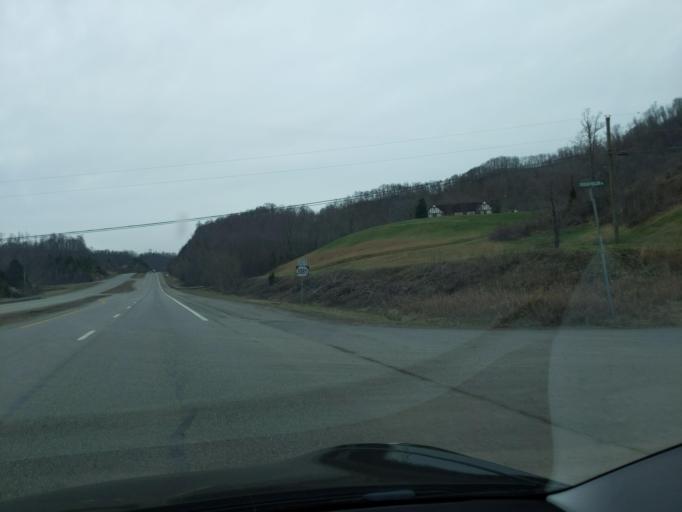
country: US
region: Kentucky
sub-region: Bell County
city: Pineville
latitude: 36.8116
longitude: -83.7641
